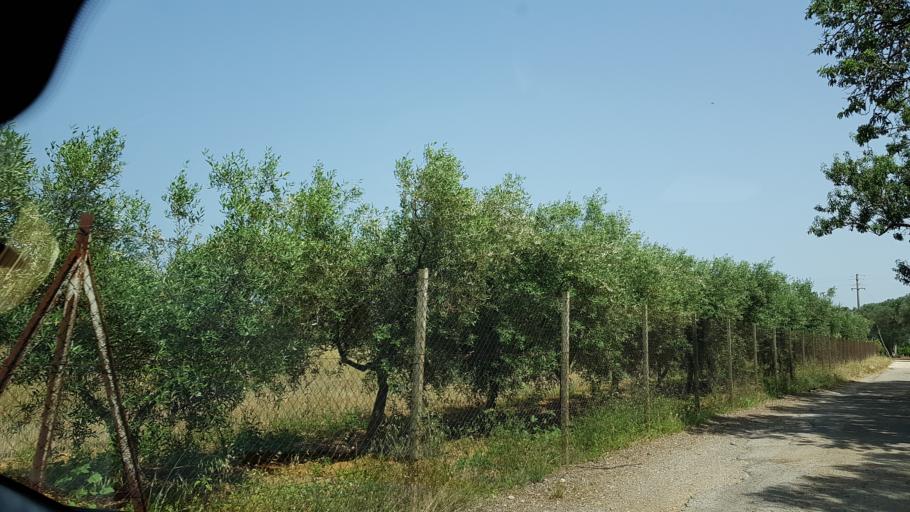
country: IT
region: Apulia
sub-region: Provincia di Brindisi
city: Mesagne
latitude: 40.5525
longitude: 17.8291
